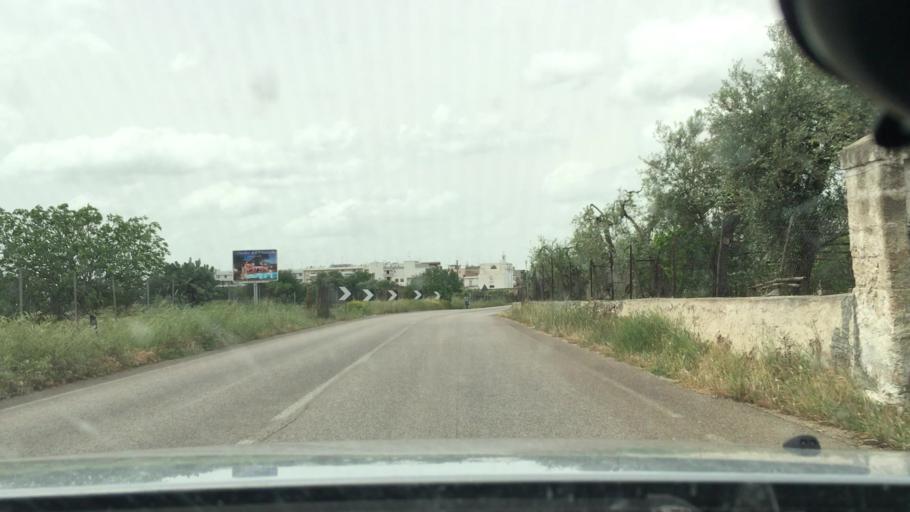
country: IT
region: Apulia
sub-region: Provincia di Bari
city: Capurso
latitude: 41.0433
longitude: 16.9350
